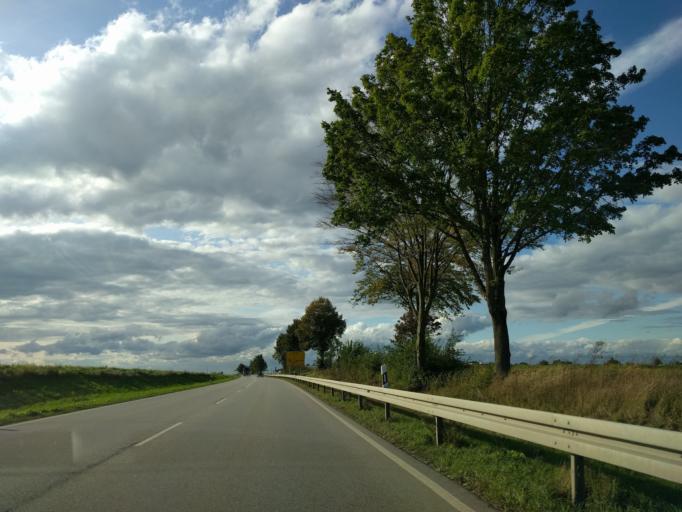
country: DE
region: Bavaria
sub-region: Lower Bavaria
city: Stephansposching
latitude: 48.7996
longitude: 12.8081
